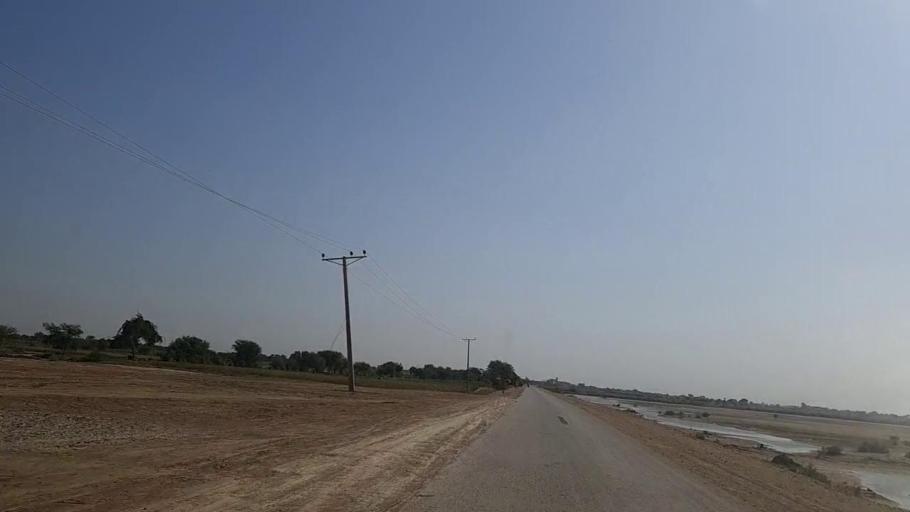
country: PK
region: Sindh
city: Mirpur Batoro
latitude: 24.6287
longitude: 68.2936
